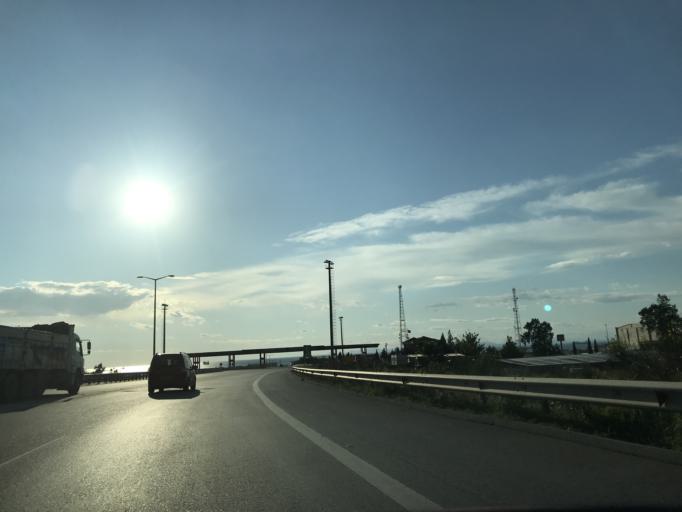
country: TR
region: Hatay
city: Guzelkoy
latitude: 36.6072
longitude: 36.2066
